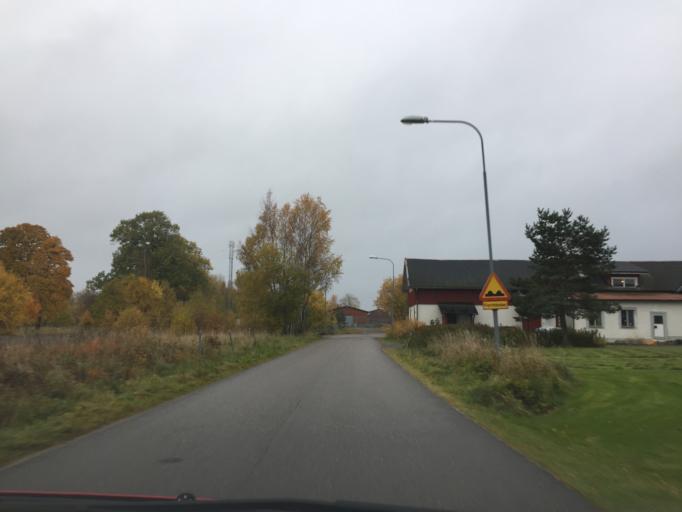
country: SE
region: Vaestra Goetaland
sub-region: Trollhattan
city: Sjuntorp
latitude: 58.1576
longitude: 12.3067
